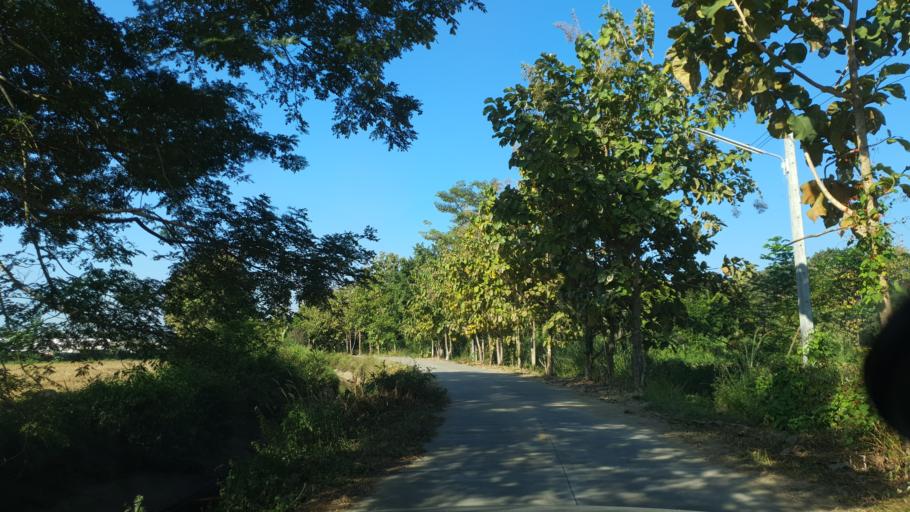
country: TH
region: Chiang Mai
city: San Kamphaeng
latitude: 18.7364
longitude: 99.1620
